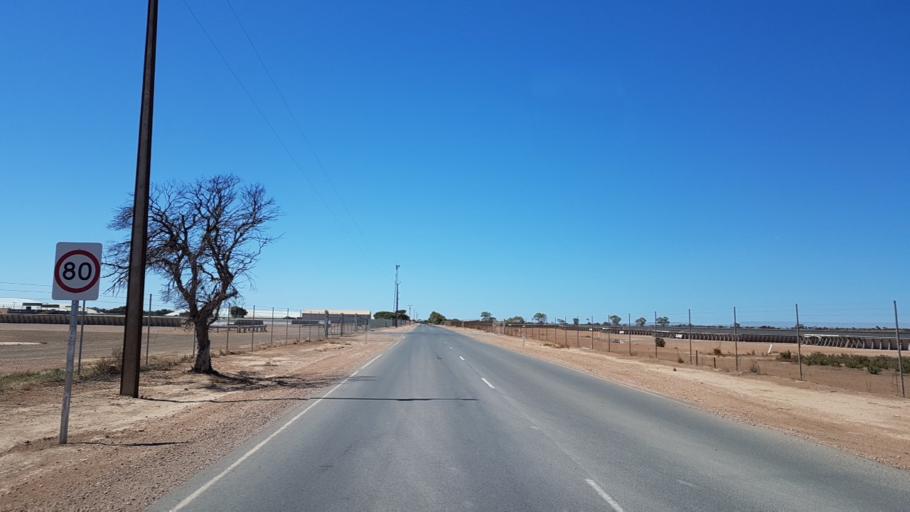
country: AU
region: South Australia
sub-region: Copper Coast
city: Wallaroo
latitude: -33.9382
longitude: 137.6101
